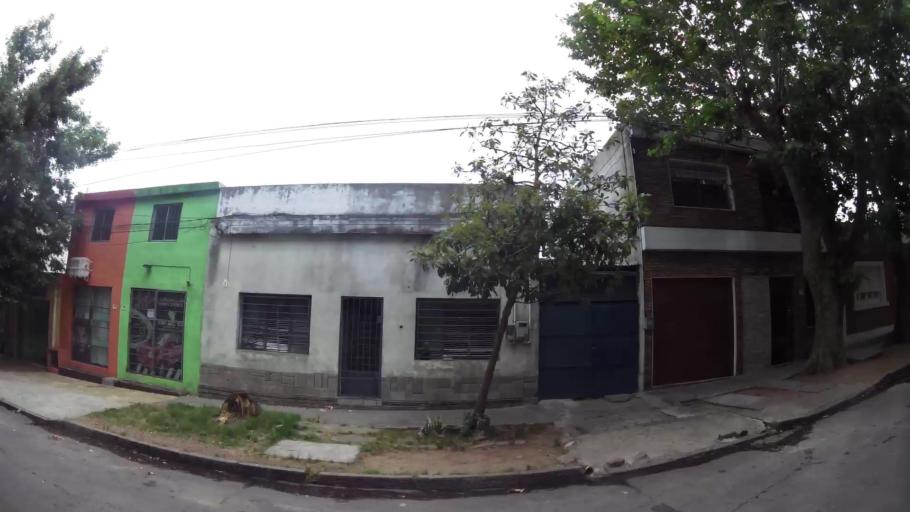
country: UY
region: Canelones
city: La Paz
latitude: -34.7634
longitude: -56.2248
